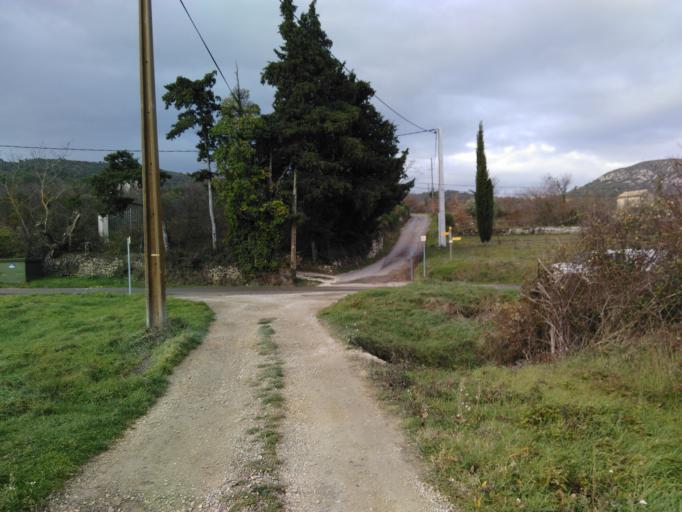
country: FR
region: Provence-Alpes-Cote d'Azur
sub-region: Departement du Vaucluse
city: Malaucene
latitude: 44.1722
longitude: 5.1190
